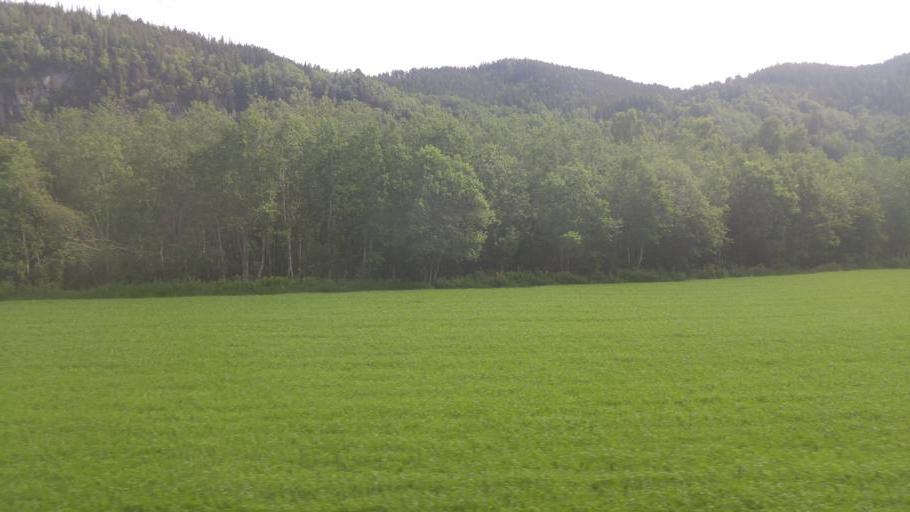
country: NO
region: Sor-Trondelag
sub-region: Midtre Gauldal
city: Storen
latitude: 63.0810
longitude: 10.2494
